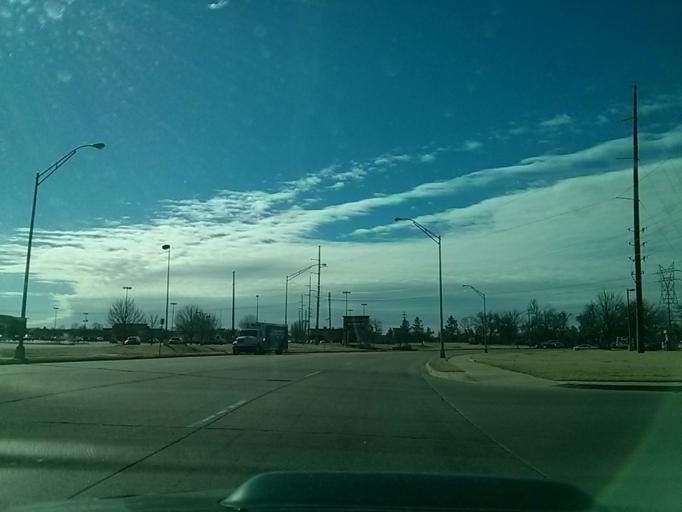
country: US
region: Oklahoma
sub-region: Tulsa County
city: Jenks
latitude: 36.0277
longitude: -95.9490
